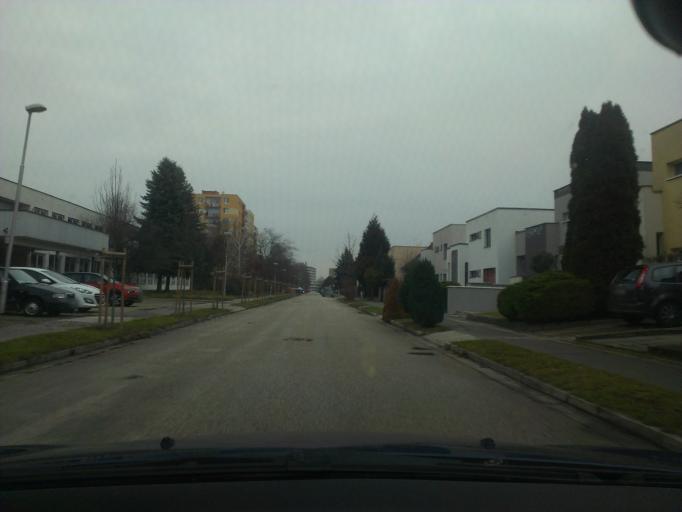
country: SK
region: Trnavsky
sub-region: Okres Trnava
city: Piestany
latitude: 48.5815
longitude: 17.8198
